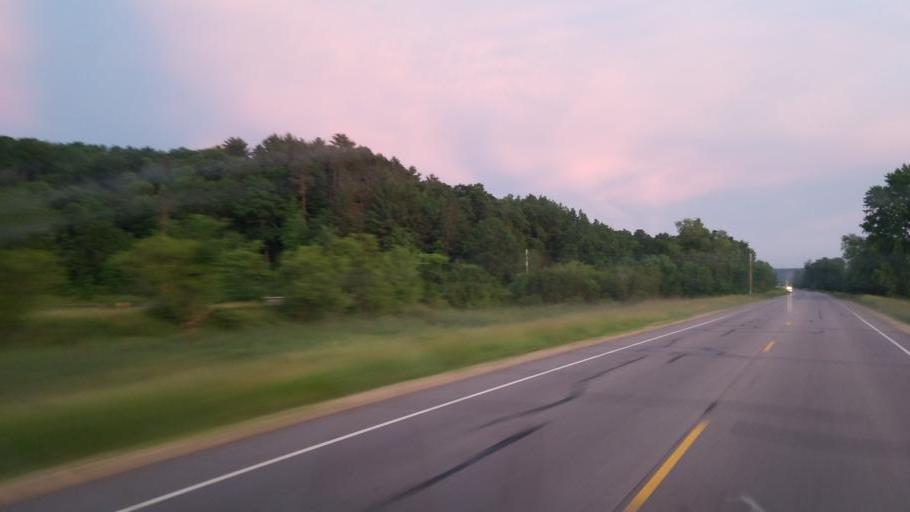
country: US
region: Wisconsin
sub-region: Juneau County
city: Elroy
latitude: 43.7010
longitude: -90.2665
